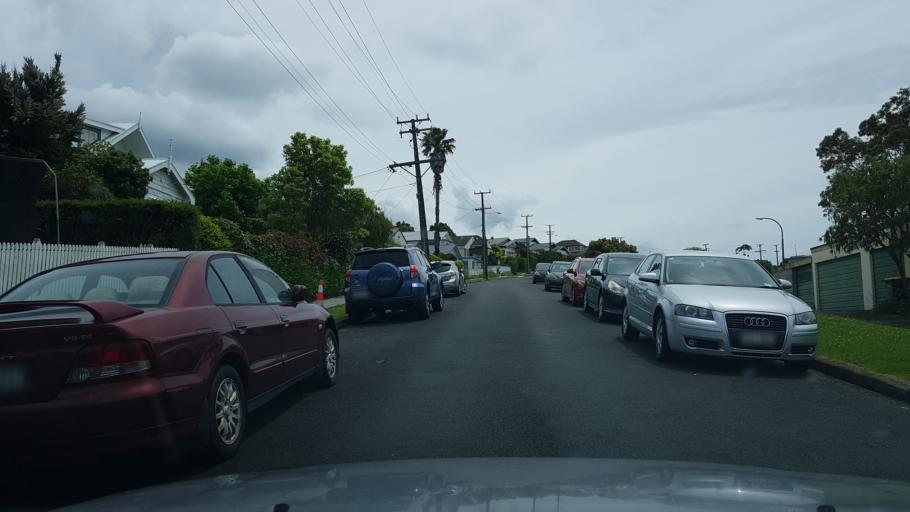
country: NZ
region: Auckland
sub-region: Auckland
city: North Shore
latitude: -36.8142
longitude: 174.7224
